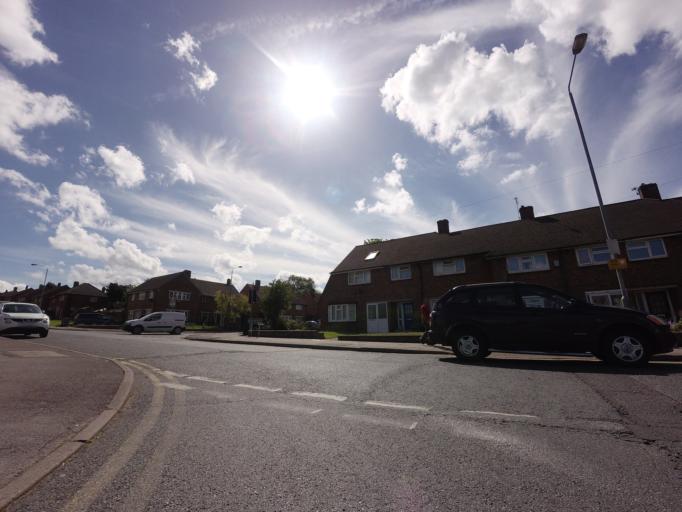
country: GB
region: England
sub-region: Greater London
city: Orpington
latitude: 51.3776
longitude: 0.1159
